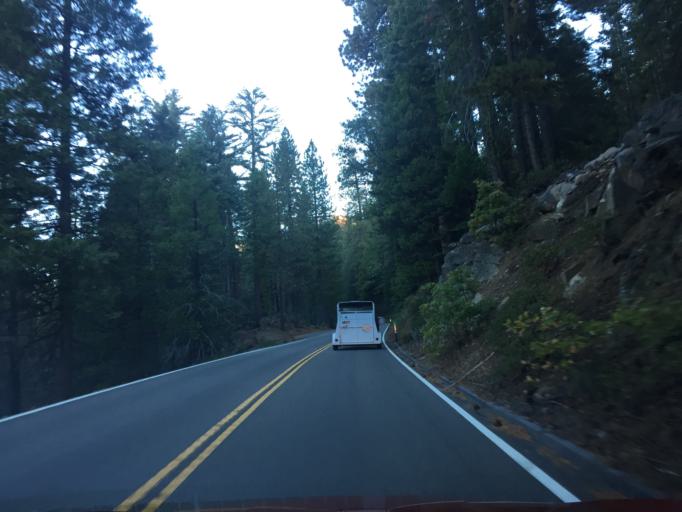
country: US
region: California
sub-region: Mariposa County
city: Yosemite Valley
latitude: 37.6410
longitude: -119.6964
